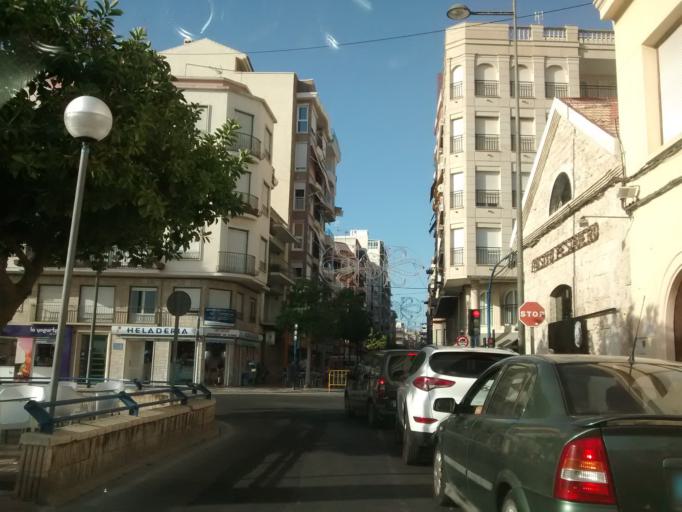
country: ES
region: Valencia
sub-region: Provincia de Alicante
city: Santa Pola
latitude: 38.1902
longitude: -0.5565
